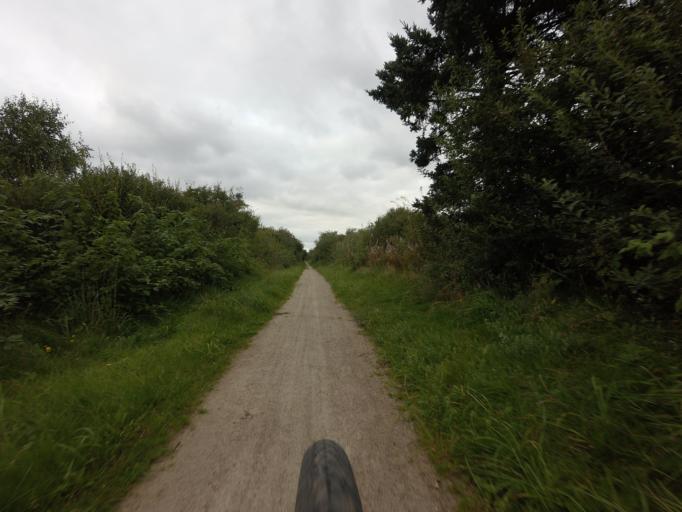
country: DK
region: South Denmark
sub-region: Billund Kommune
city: Billund
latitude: 55.8212
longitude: 9.0317
